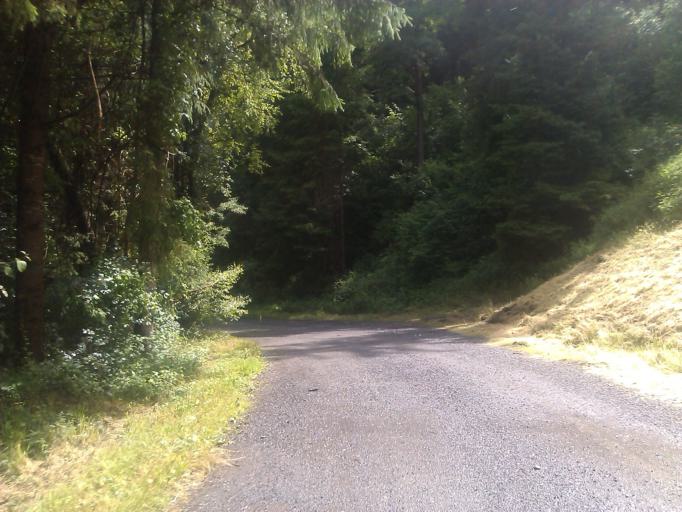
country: AT
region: Tyrol
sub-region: Politischer Bezirk Landeck
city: Prutz
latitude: 47.1124
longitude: 10.6486
